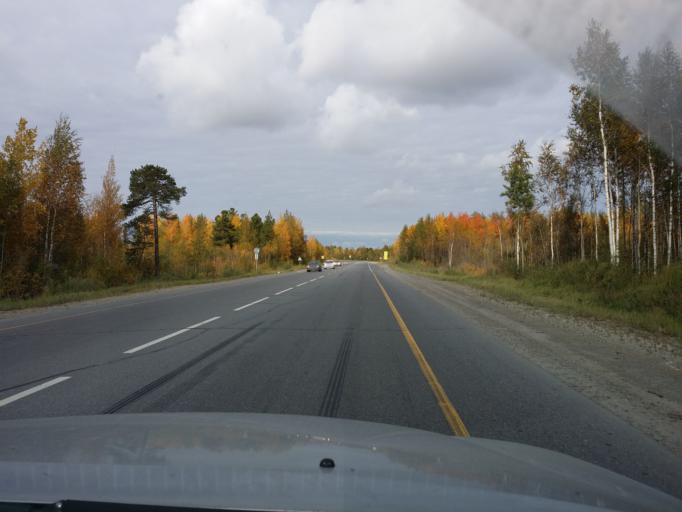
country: RU
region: Khanty-Mansiyskiy Avtonomnyy Okrug
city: Megion
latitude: 61.1074
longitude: 76.0407
